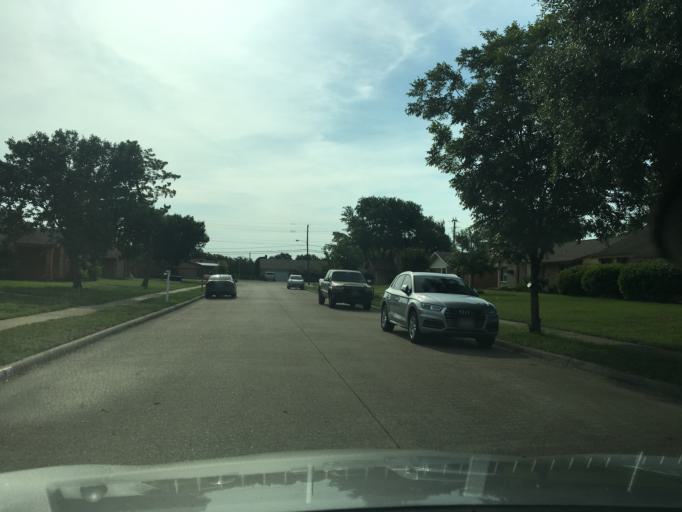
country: US
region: Texas
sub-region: Dallas County
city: Garland
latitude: 32.9618
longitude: -96.6710
